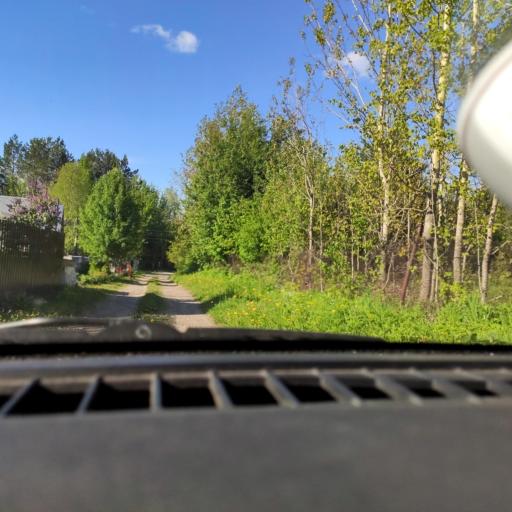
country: RU
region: Perm
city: Polazna
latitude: 58.2936
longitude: 56.1309
